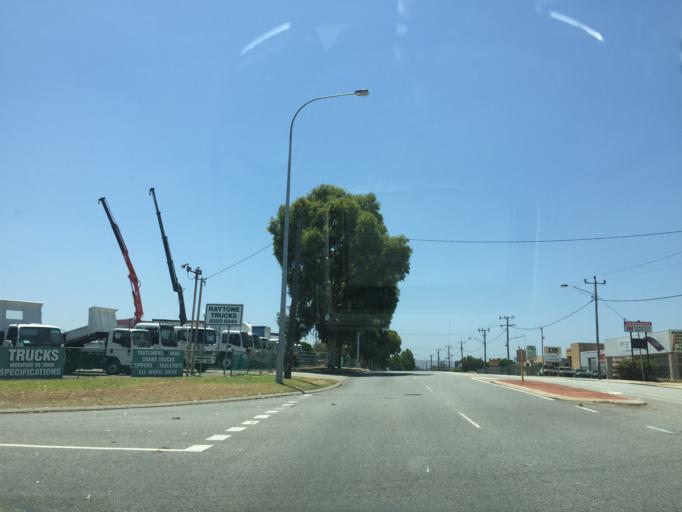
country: AU
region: Western Australia
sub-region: Canning
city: Bentley
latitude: -31.9947
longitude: 115.9320
